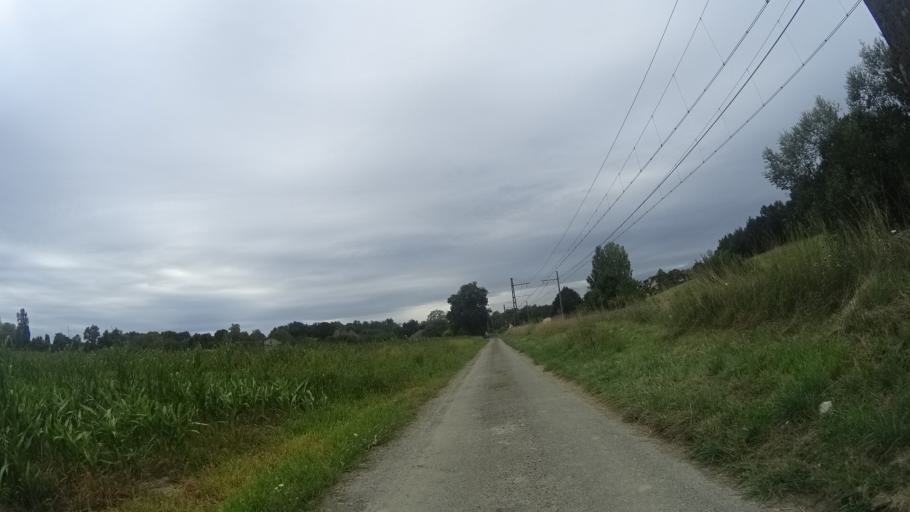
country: FR
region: Aquitaine
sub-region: Departement des Pyrenees-Atlantiques
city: Orthez
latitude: 43.4690
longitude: -0.7233
